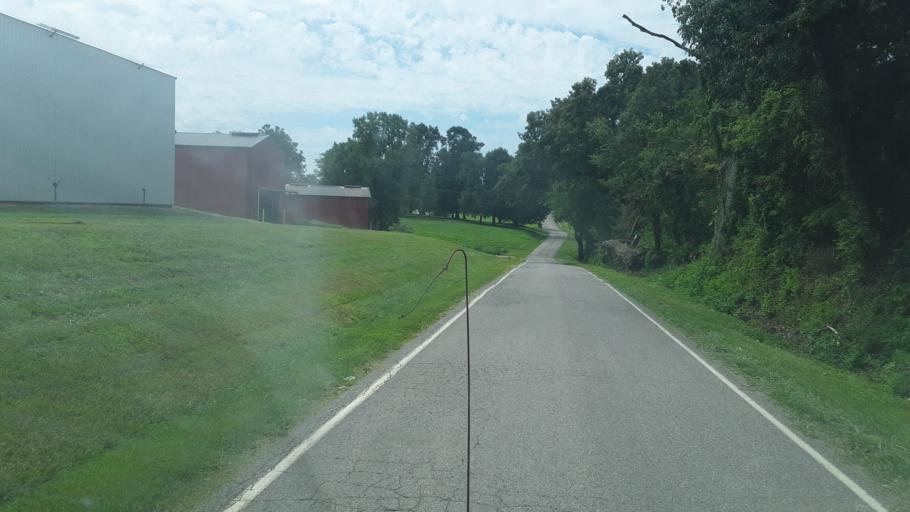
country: US
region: Kentucky
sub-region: Christian County
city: Oak Grove
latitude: 36.6501
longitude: -87.3440
